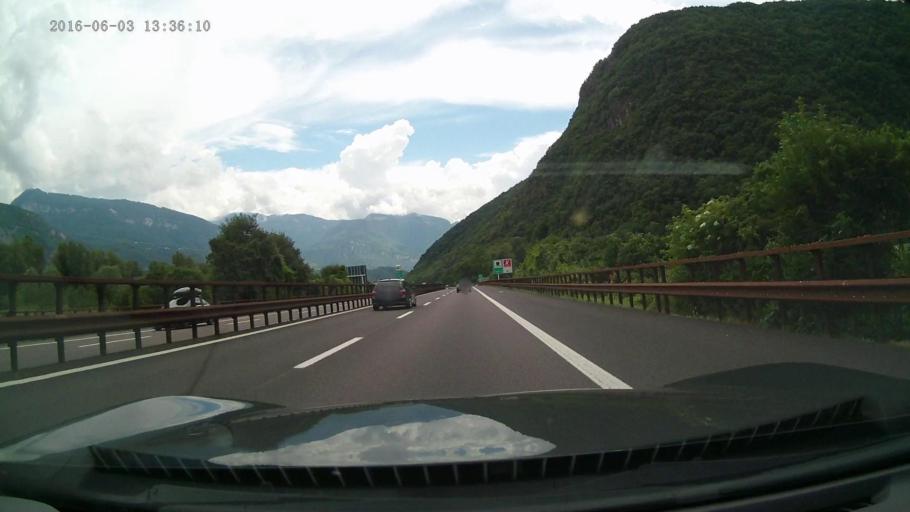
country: IT
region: Trentino-Alto Adige
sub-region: Bolzano
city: Ora
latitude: 46.3763
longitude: 11.2908
